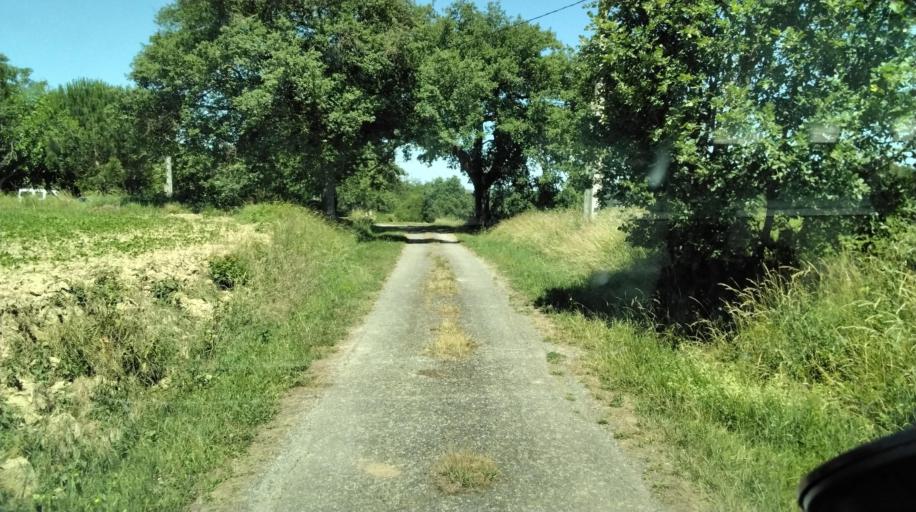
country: FR
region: Midi-Pyrenees
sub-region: Departement de la Haute-Garonne
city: Sainte-Foy-de-Peyrolieres
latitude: 43.4757
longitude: 1.0807
